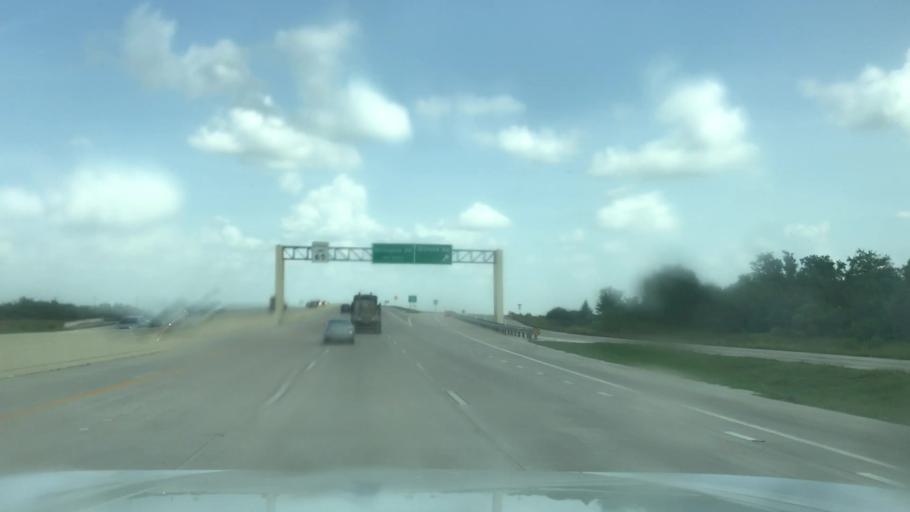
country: US
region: Texas
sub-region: Waller County
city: Waller
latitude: 30.0590
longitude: -95.8962
